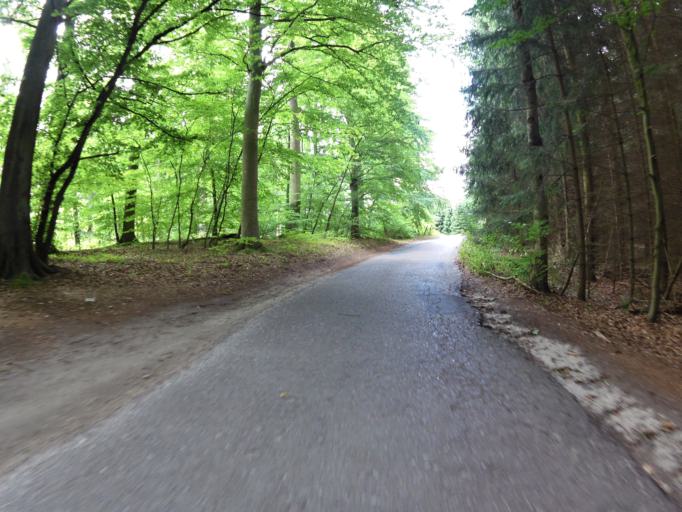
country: DE
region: Mecklenburg-Vorpommern
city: Seebad Bansin
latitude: 53.9830
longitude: 14.1091
